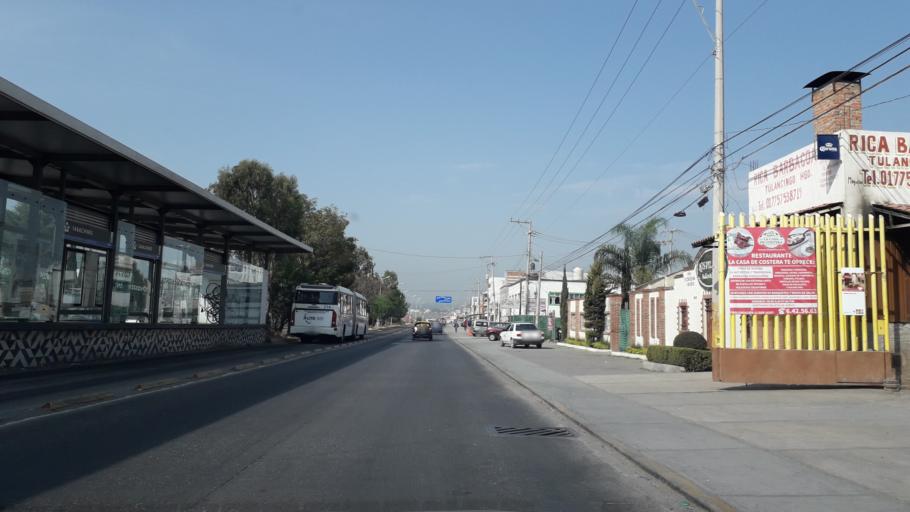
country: MX
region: Puebla
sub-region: Puebla
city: El Capulo (La Quebradora)
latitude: 18.9741
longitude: -98.2600
